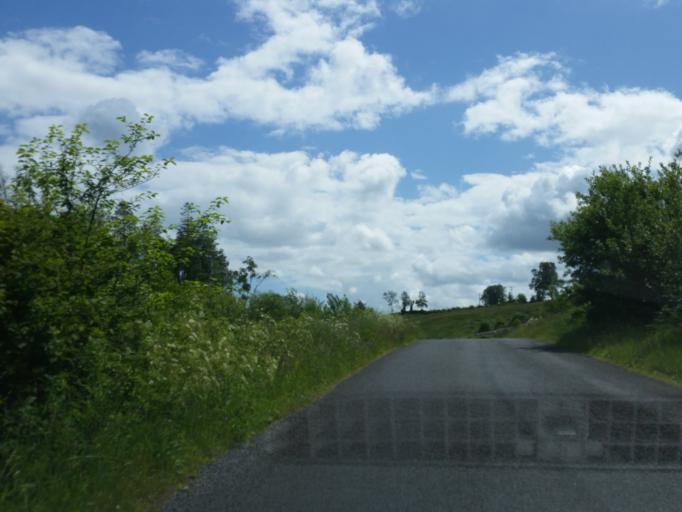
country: GB
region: Northern Ireland
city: Fivemiletown
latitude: 54.3546
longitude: -7.3016
